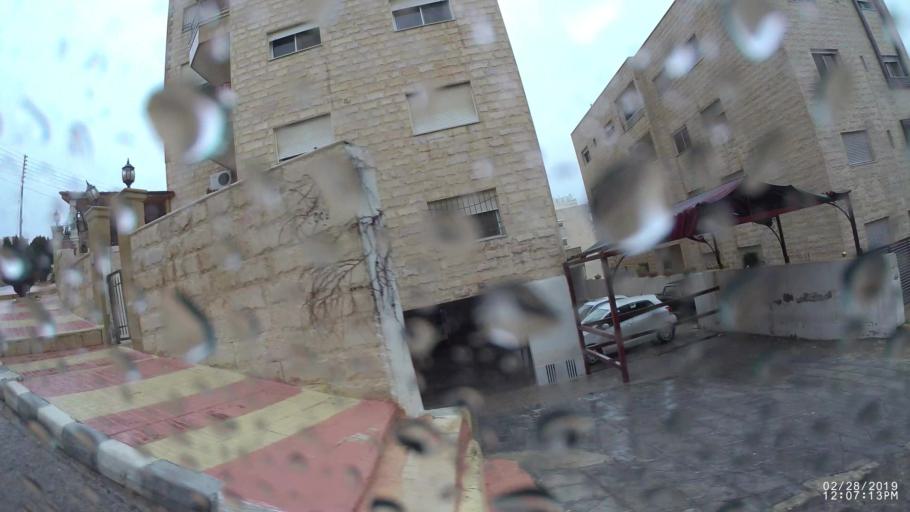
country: JO
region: Amman
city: Al Jubayhah
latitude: 32.0209
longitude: 35.8913
